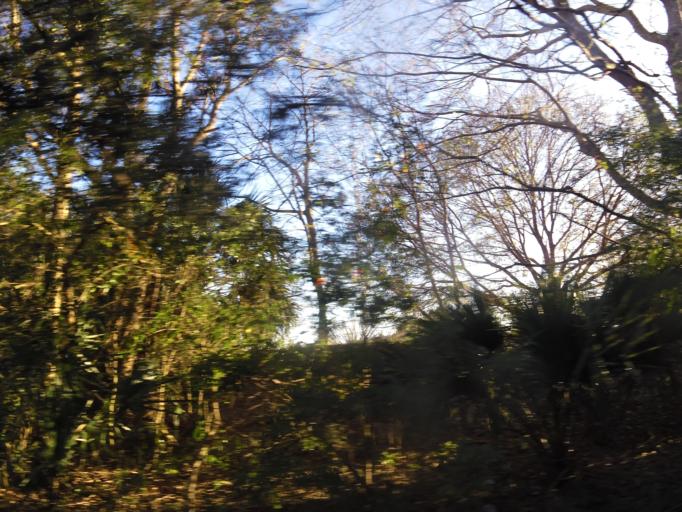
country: US
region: Florida
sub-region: Saint Johns County
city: Fruit Cove
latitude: 30.2005
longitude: -81.5912
